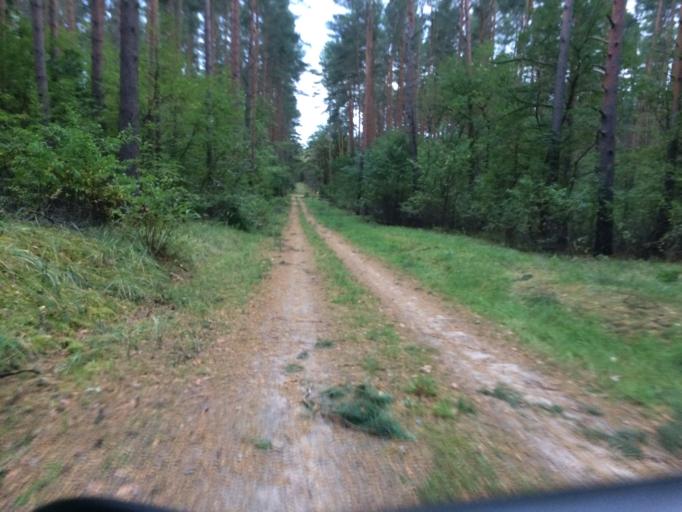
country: DE
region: Brandenburg
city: Birkenwerder
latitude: 52.7020
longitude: 13.3119
